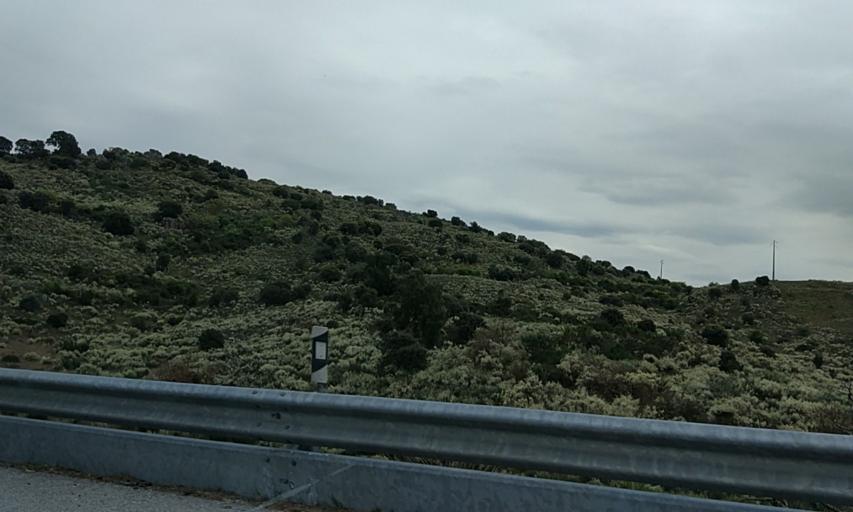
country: PT
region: Guarda
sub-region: Celorico da Beira
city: Celorico da Beira
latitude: 40.6258
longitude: -7.3652
